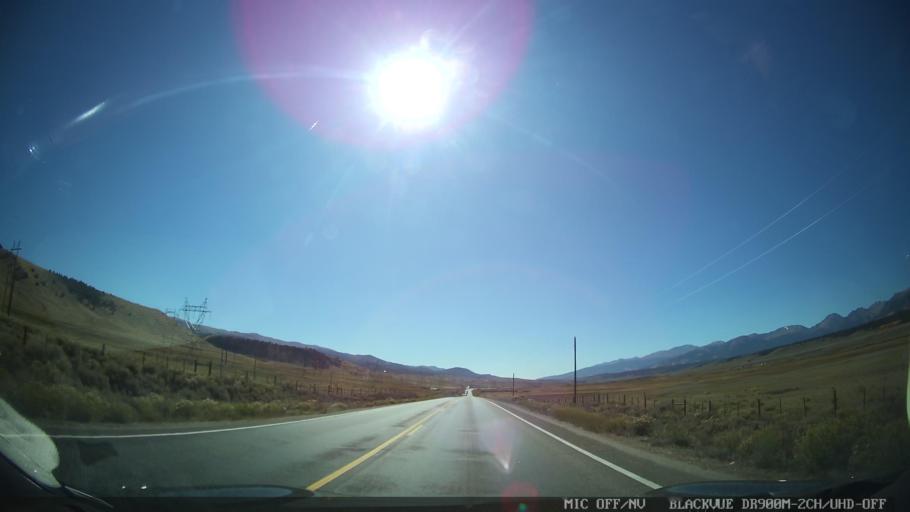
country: US
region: Colorado
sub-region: Lake County
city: Leadville
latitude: 39.1838
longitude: -106.3280
